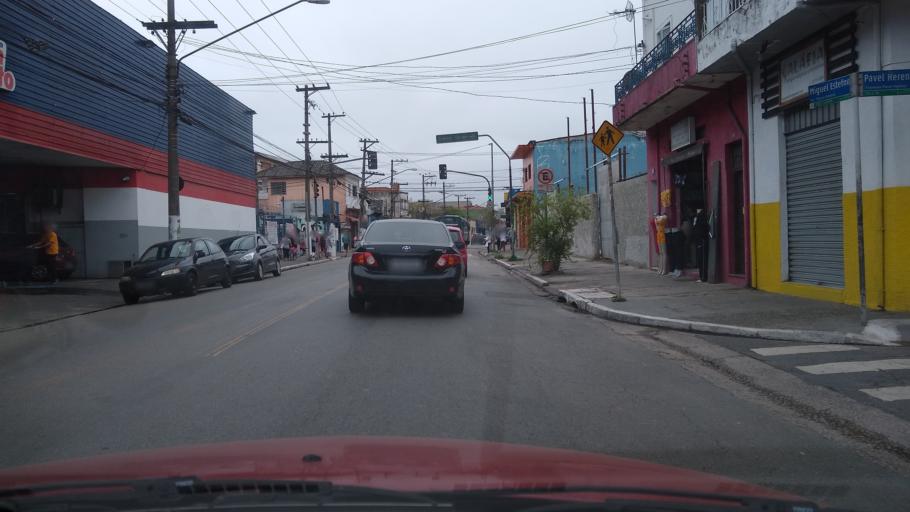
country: BR
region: Sao Paulo
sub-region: Diadema
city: Diadema
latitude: -23.6341
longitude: -46.6274
